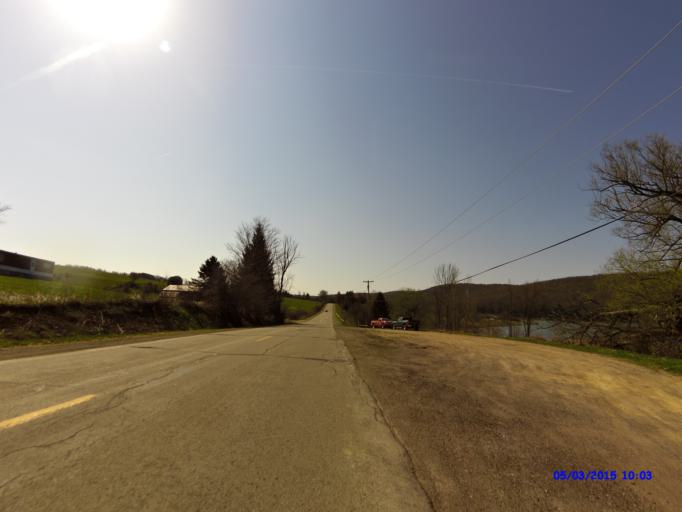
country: US
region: New York
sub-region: Cattaraugus County
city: Franklinville
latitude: 42.3248
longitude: -78.4360
